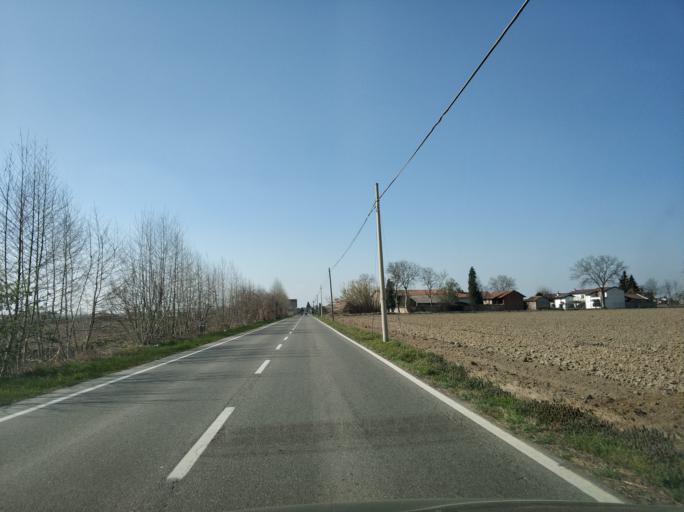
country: IT
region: Piedmont
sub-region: Provincia di Vercelli
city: Borgo Vercelli
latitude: 45.3316
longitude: 8.4581
